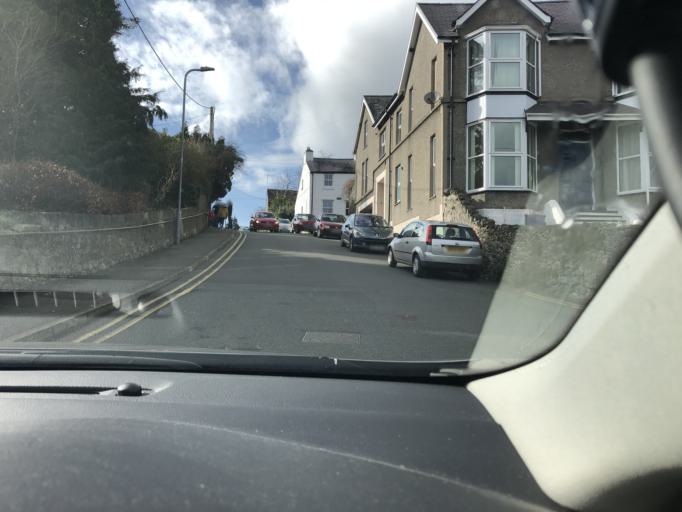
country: GB
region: Wales
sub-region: Anglesey
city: Menai Bridge
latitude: 53.2270
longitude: -4.1646
